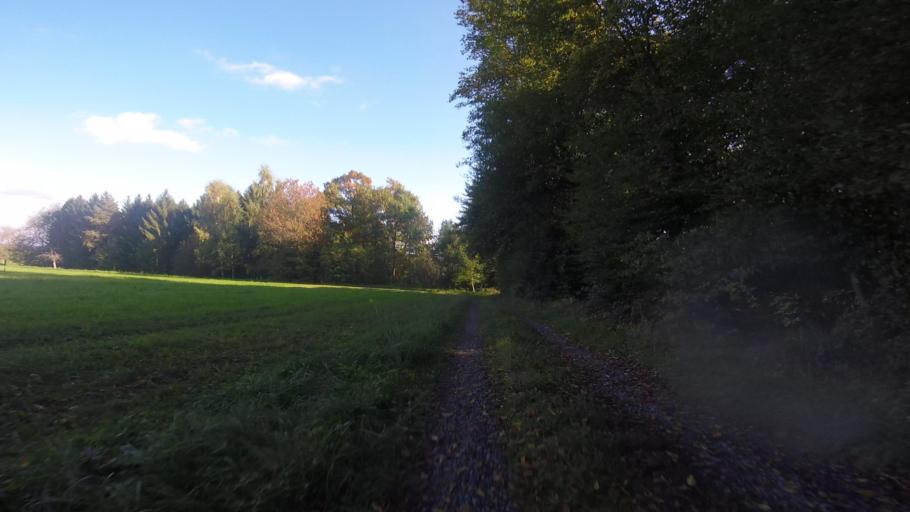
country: DE
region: Baden-Wuerttemberg
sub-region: Regierungsbezirk Stuttgart
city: Oberstenfeld
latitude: 48.9999
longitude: 9.3364
